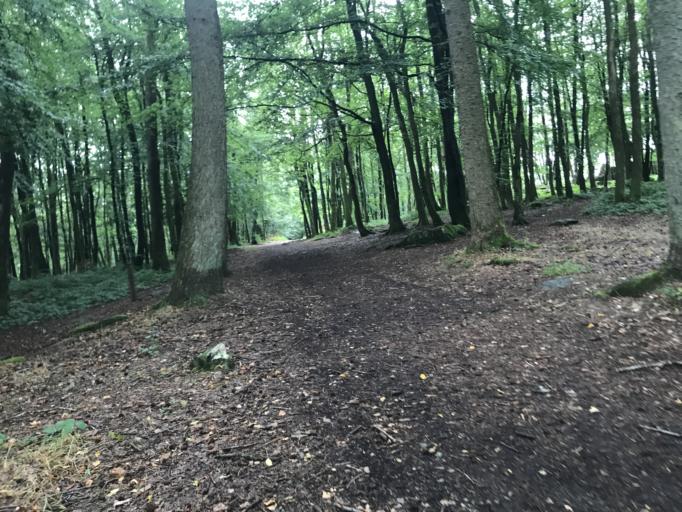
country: FR
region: Champagne-Ardenne
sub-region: Departement des Ardennes
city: Thilay
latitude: 49.8917
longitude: 4.7837
